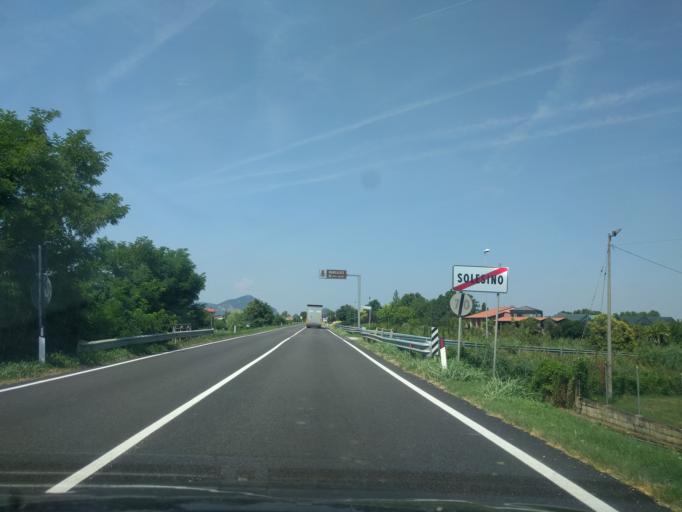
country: IT
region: Veneto
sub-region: Provincia di Padova
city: Solesino
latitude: 45.1903
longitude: 11.7559
